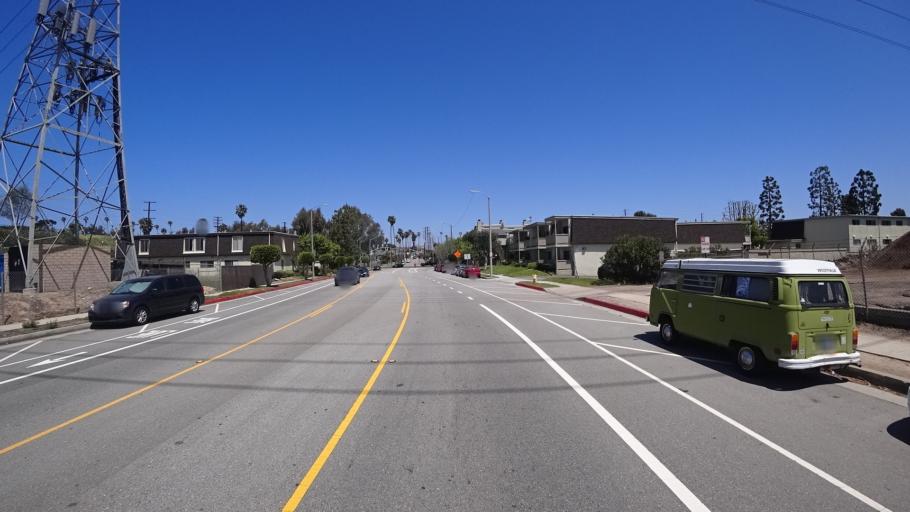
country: US
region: California
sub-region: Los Angeles County
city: Redondo Beach
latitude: 33.8571
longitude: -118.3747
